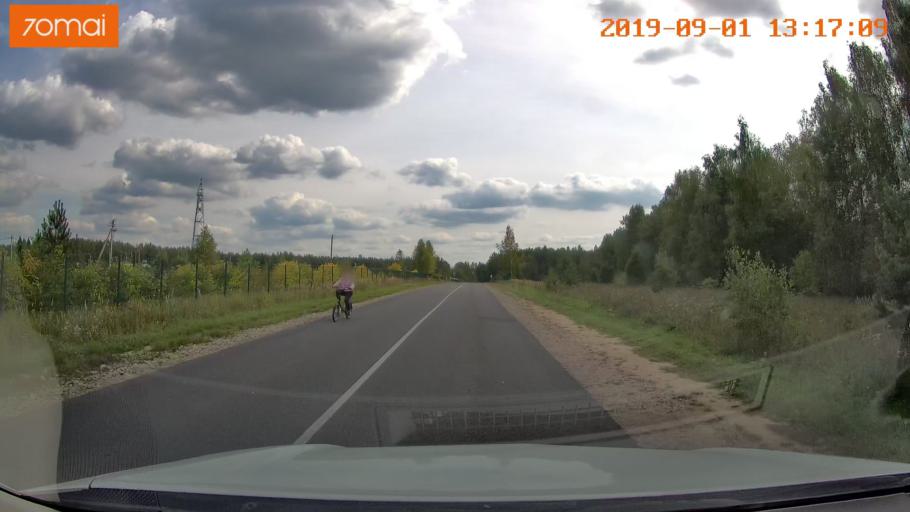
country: RU
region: Kaluga
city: Maloyaroslavets
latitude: 54.9382
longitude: 36.4623
